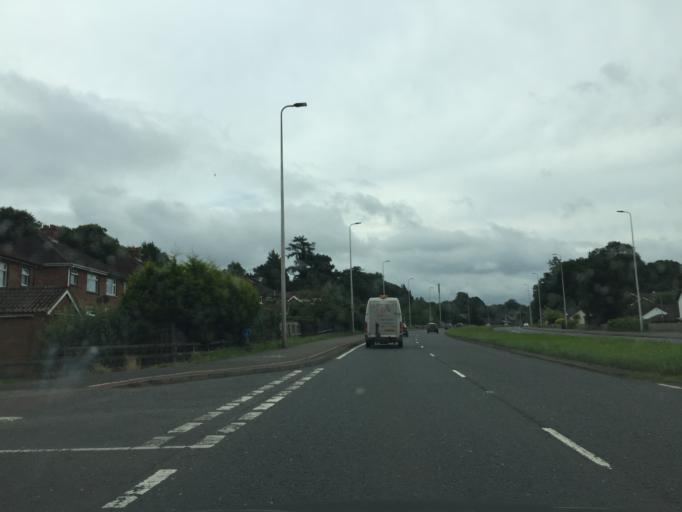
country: GB
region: Northern Ireland
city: Holywood
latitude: 54.6133
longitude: -5.8585
